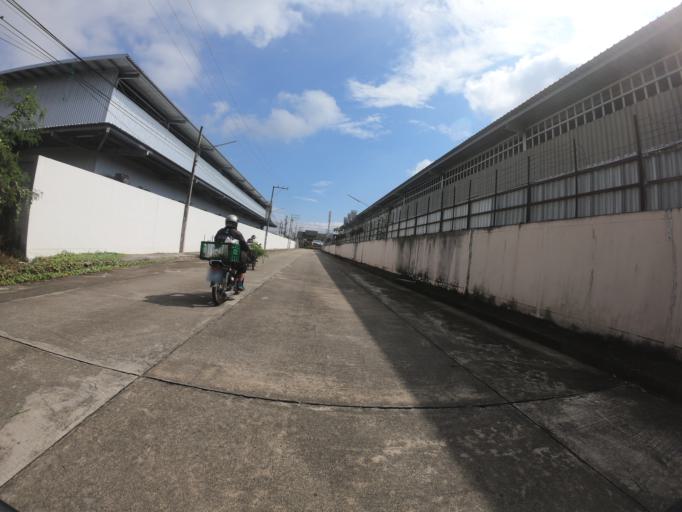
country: TH
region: Chiang Mai
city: Hang Dong
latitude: 18.7110
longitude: 98.9356
